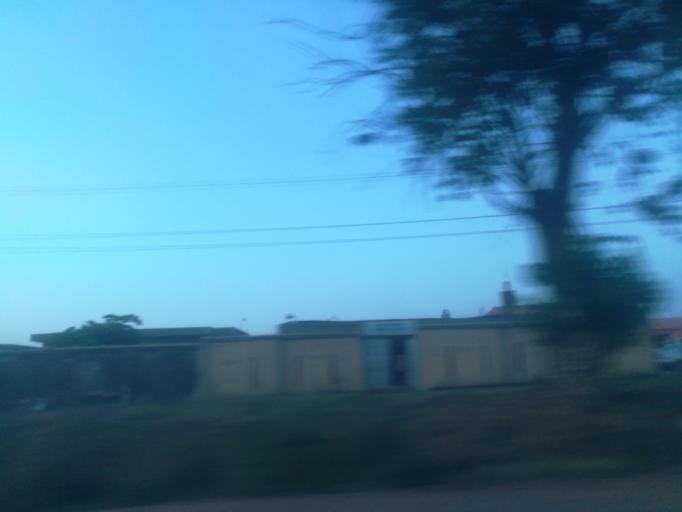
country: NG
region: Ogun
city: Abeokuta
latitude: 7.1795
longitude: 3.4083
